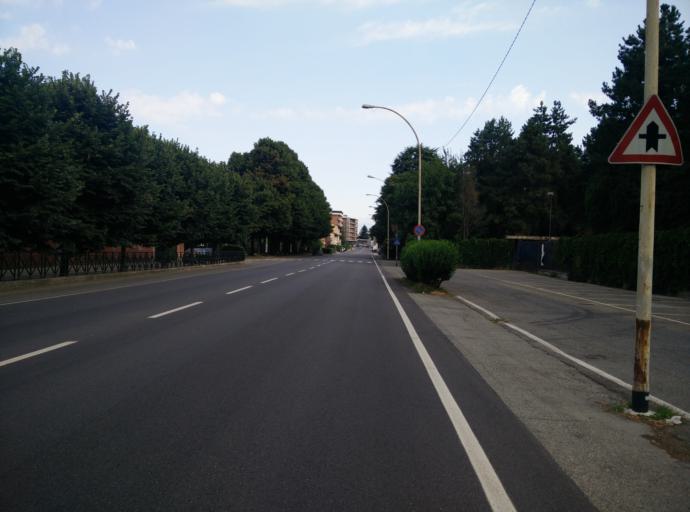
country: IT
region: Piedmont
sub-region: Provincia di Torino
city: Moncalieri
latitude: 45.0129
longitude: 7.6836
